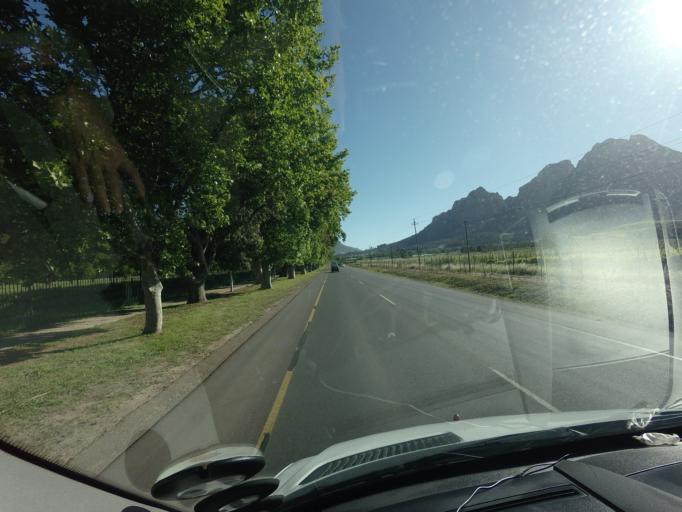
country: ZA
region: Western Cape
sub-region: Cape Winelands District Municipality
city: Stellenbosch
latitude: -33.8802
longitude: 18.9708
